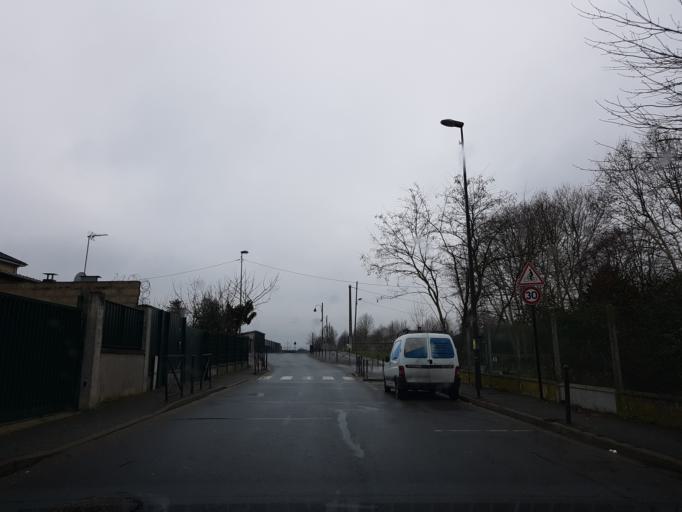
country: FR
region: Ile-de-France
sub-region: Departement du Val-de-Marne
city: Thiais
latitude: 48.7764
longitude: 2.3928
